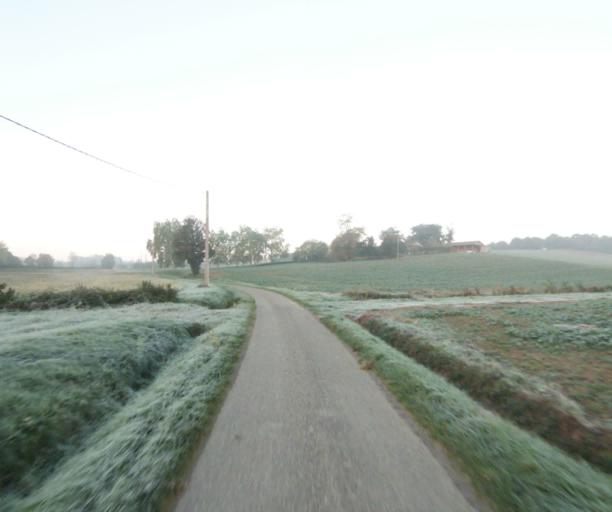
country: FR
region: Midi-Pyrenees
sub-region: Departement du Gers
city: Vic-Fezensac
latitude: 43.7769
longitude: 0.2383
